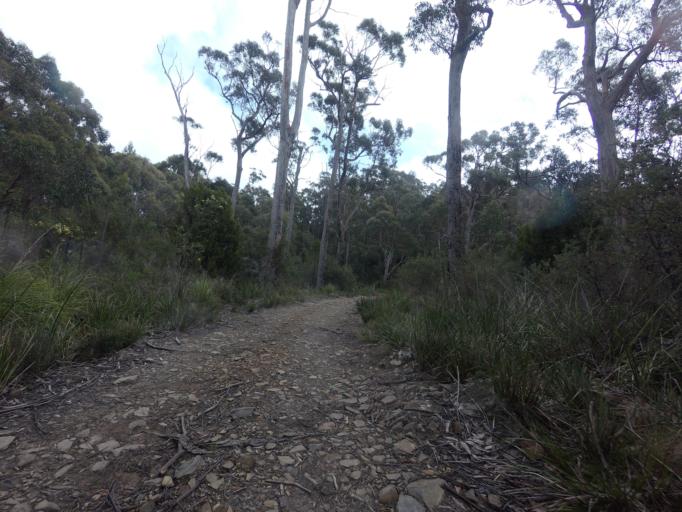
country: AU
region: Tasmania
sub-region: Huon Valley
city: Geeveston
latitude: -43.4727
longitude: 146.9336
